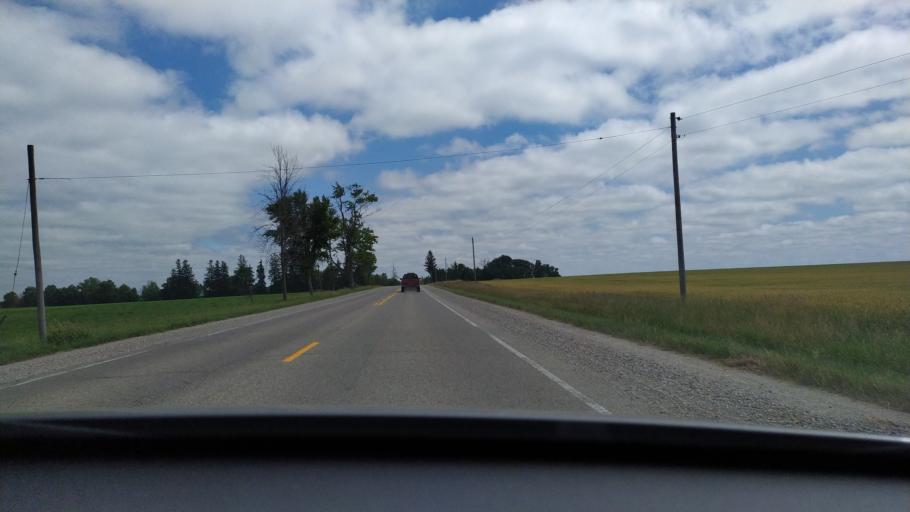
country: CA
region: Ontario
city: Stratford
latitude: 43.3070
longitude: -80.9794
